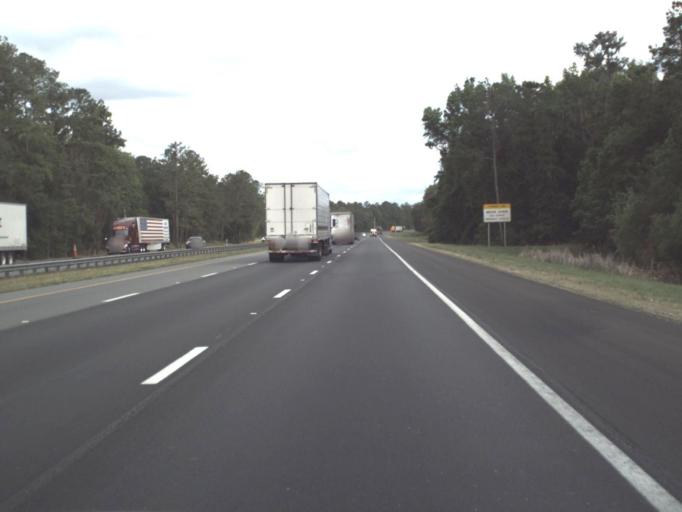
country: US
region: Florida
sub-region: Marion County
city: Citra
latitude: 29.4713
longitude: -82.2770
